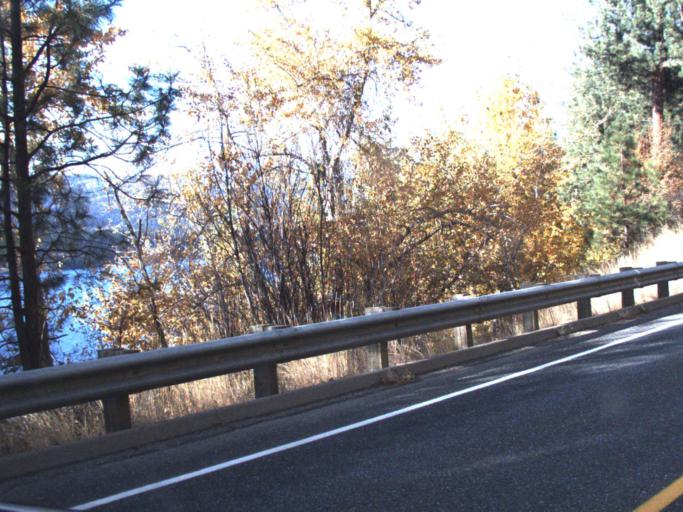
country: US
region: Washington
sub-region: Stevens County
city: Kettle Falls
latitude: 48.5311
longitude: -118.1348
